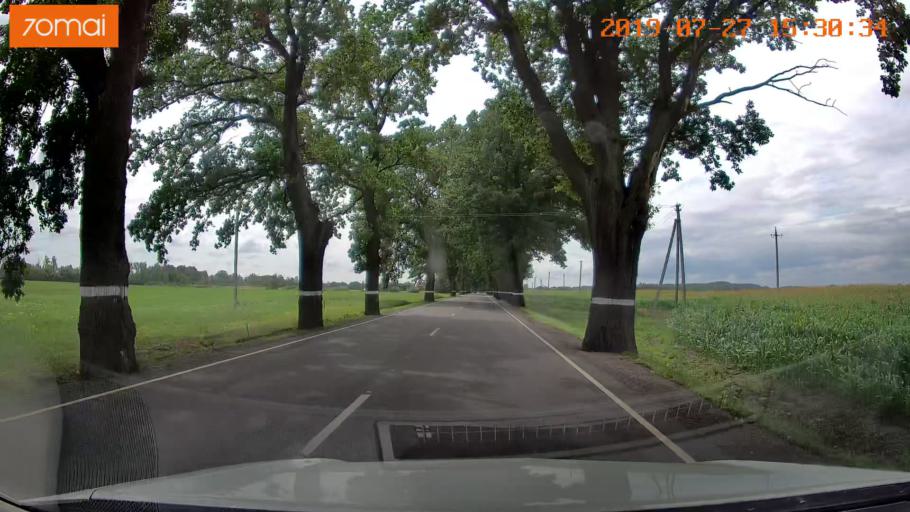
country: RU
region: Kaliningrad
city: Nesterov
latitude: 54.6272
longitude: 22.5093
